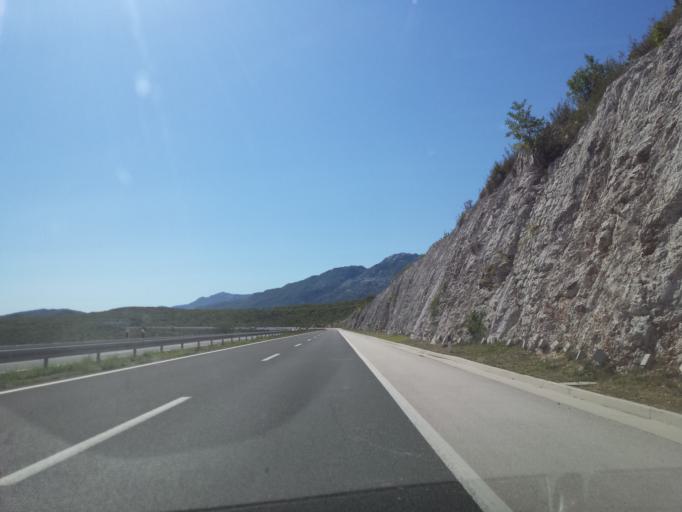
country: HR
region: Splitsko-Dalmatinska
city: Dugopolje
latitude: 43.5966
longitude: 16.6252
